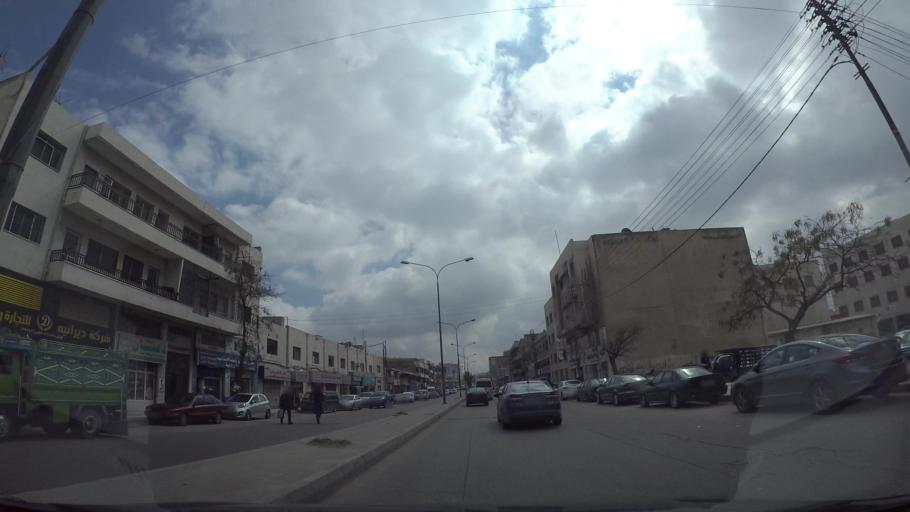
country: JO
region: Amman
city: Al Quwaysimah
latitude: 31.9239
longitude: 35.9380
